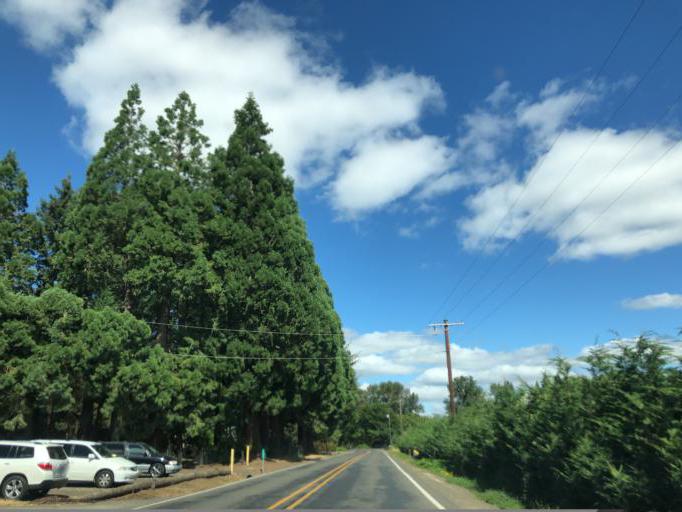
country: US
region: Oregon
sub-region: Marion County
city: Mount Angel
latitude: 45.1005
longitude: -122.7434
